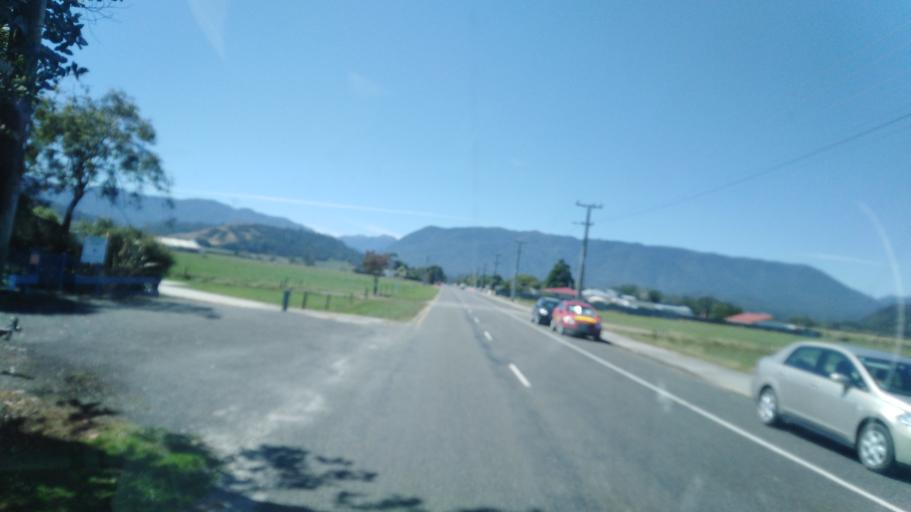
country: NZ
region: West Coast
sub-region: Buller District
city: Westport
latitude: -41.2480
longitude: 172.1136
